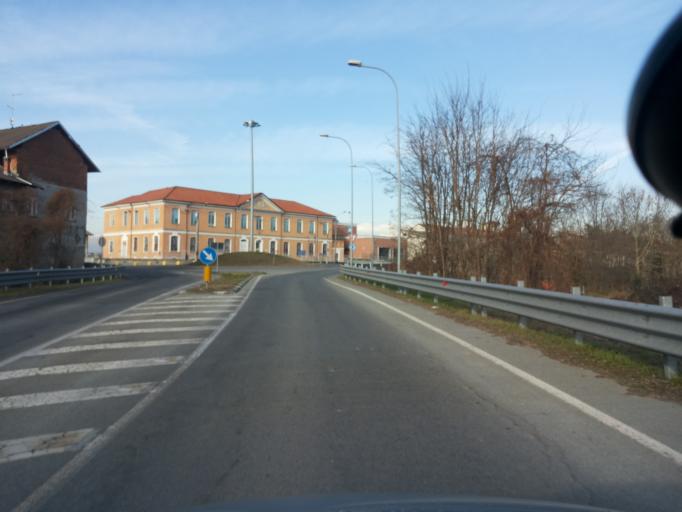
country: IT
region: Piedmont
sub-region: Provincia di Vercelli
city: Arborio
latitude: 45.4986
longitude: 8.3905
